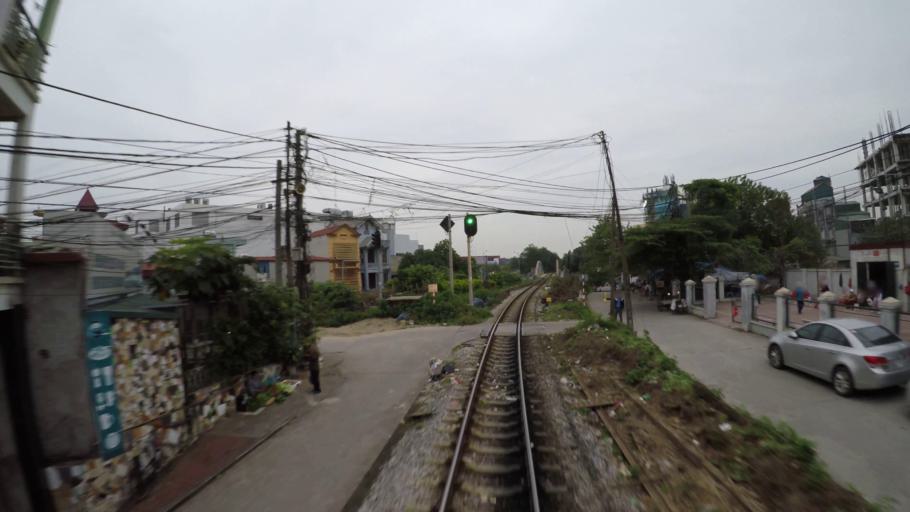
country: VN
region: Ha Noi
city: Trau Quy
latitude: 21.0199
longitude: 105.9398
